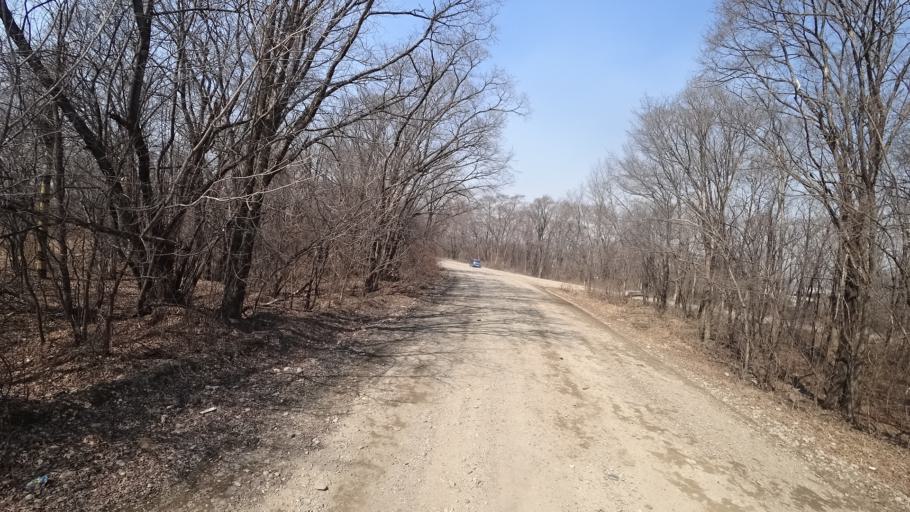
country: RU
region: Amur
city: Novobureyskiy
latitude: 49.7894
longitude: 129.9080
